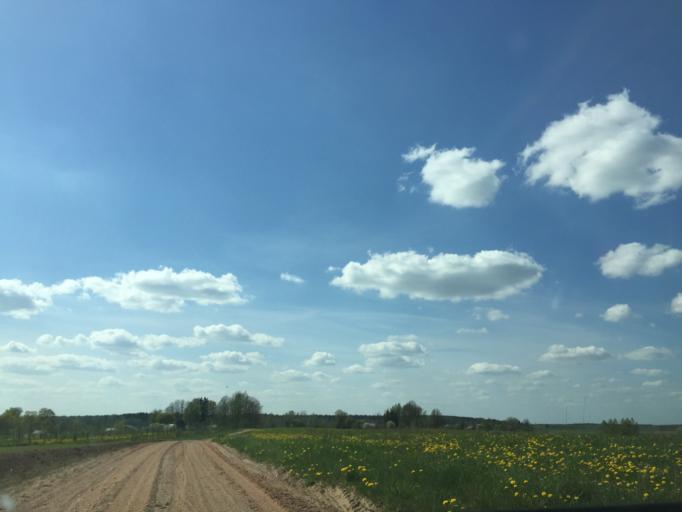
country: LV
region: Vecumnieki
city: Vecumnieki
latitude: 56.4820
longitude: 24.5587
